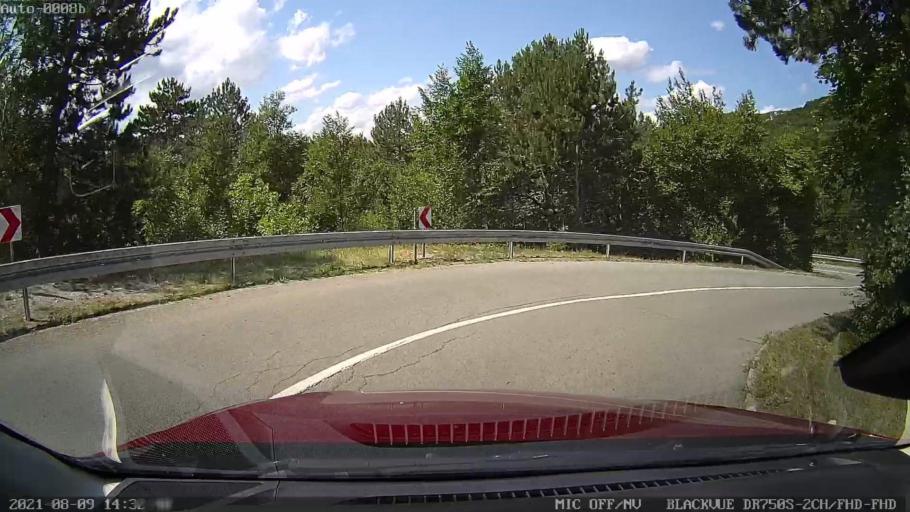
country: HR
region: Istarska
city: Lovran
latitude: 45.3114
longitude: 14.1901
